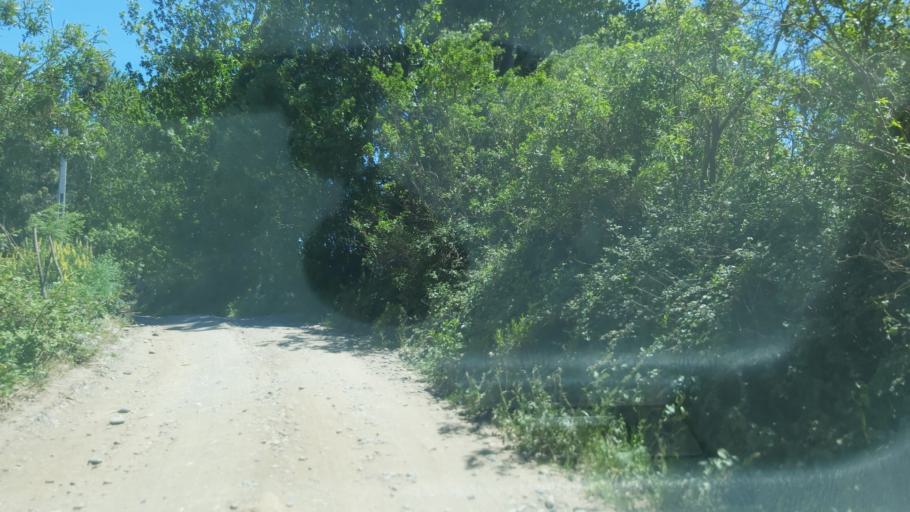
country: CL
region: Maule
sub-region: Provincia de Talca
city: Constitucion
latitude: -35.1621
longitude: -72.2663
